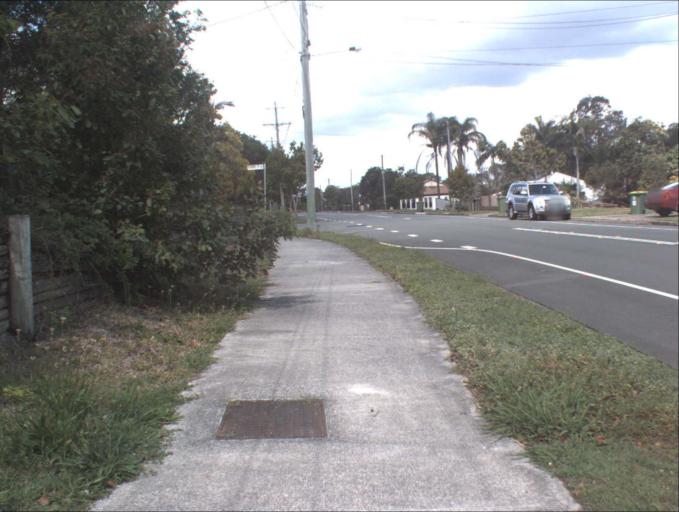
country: AU
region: Queensland
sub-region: Logan
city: Waterford West
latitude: -27.6847
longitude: 153.1485
